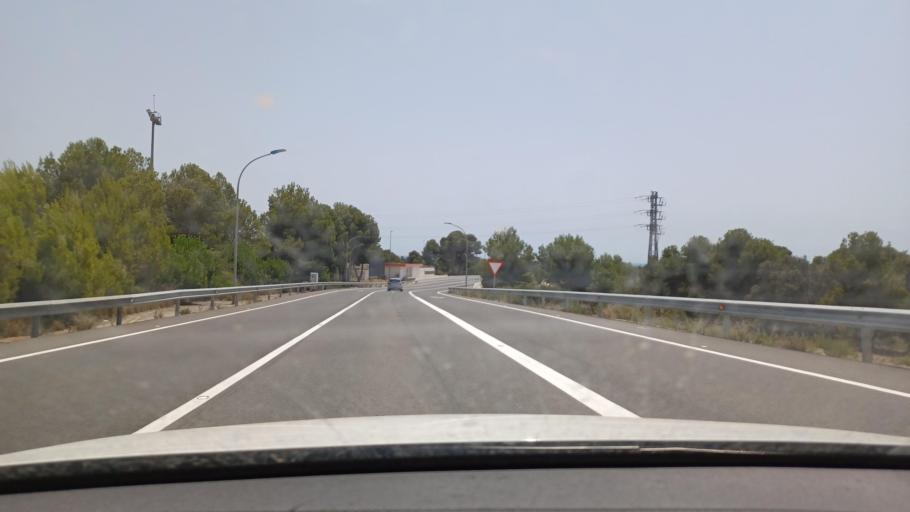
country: ES
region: Catalonia
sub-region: Provincia de Tarragona
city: Cambrils
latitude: 41.0799
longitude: 1.0414
